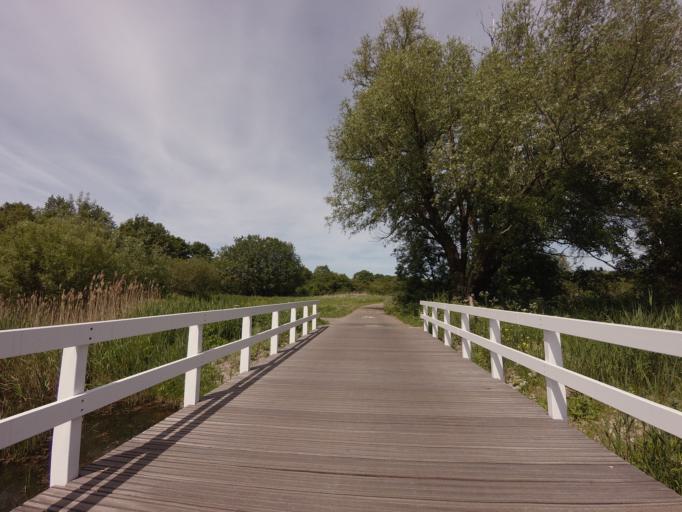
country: NL
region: North Holland
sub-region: Gemeente Zaanstad
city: Zaandam
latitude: 52.3859
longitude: 4.7778
